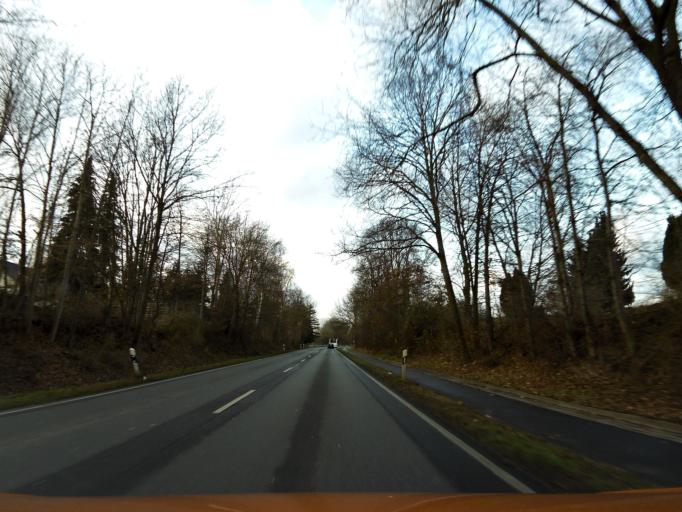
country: DE
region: Lower Saxony
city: Wolfsburg
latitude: 52.4039
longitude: 10.8328
